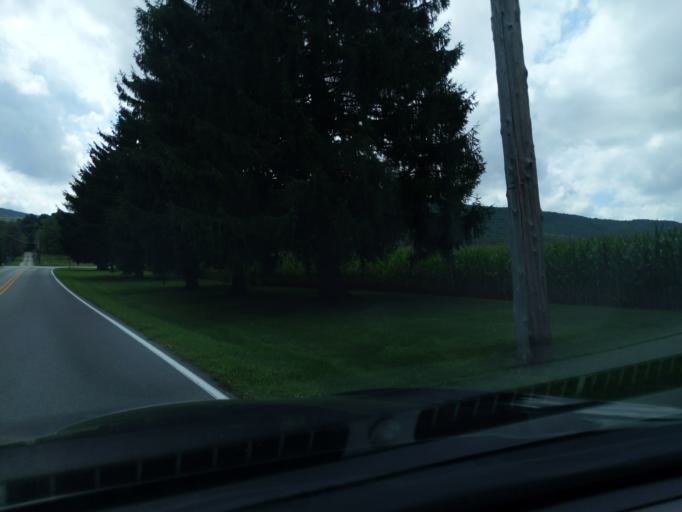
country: US
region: Pennsylvania
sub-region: Blair County
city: Hollidaysburg
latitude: 40.3938
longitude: -78.4001
